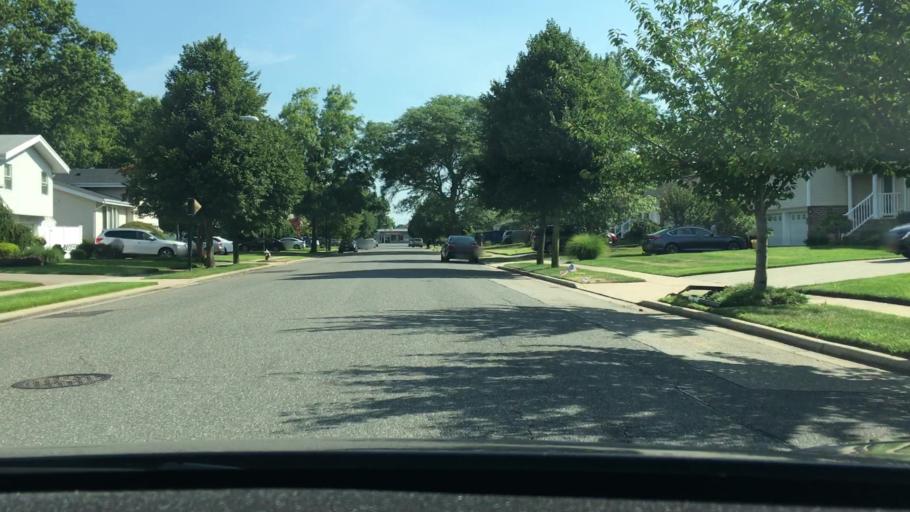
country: US
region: New York
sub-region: Nassau County
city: Jericho
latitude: 40.7964
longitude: -73.5191
